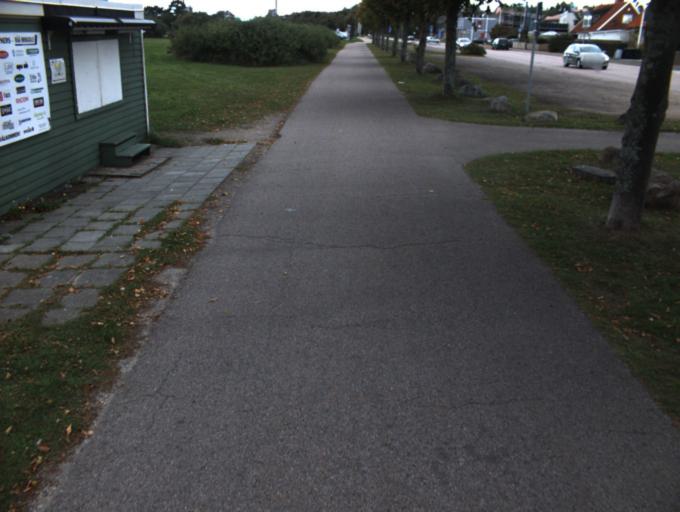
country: SE
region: Skane
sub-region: Helsingborg
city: Rydeback
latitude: 56.0016
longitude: 12.7327
